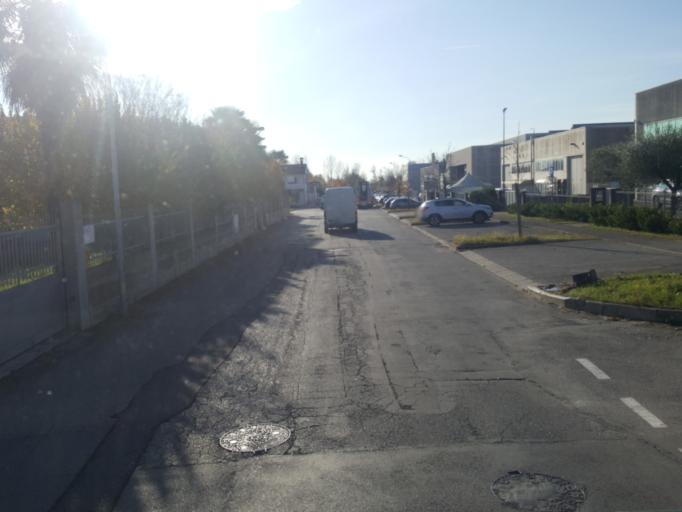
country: IT
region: Veneto
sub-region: Provincia di Treviso
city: One
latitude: 45.7833
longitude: 11.8879
